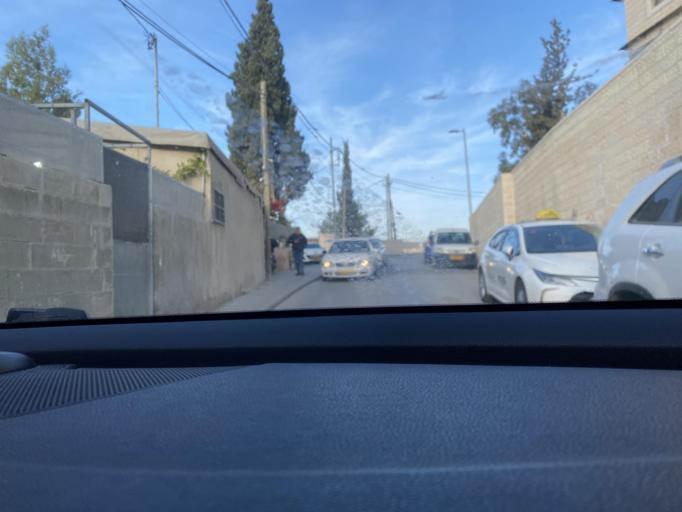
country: PS
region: West Bank
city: Ash Shaykh Sa`d
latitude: 31.7381
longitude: 35.2437
